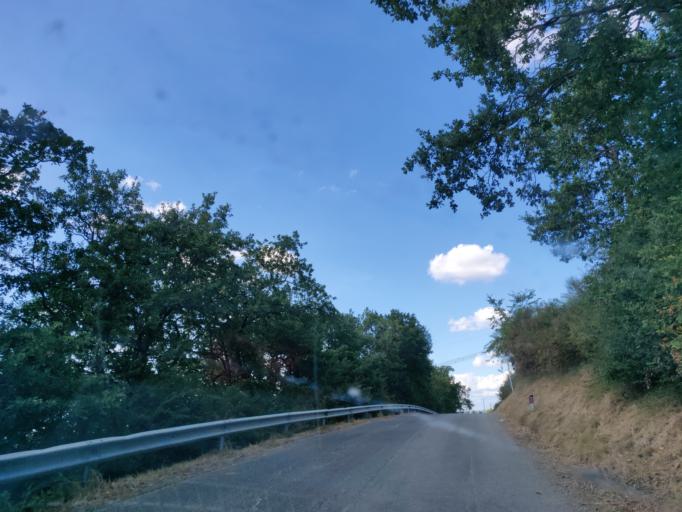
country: IT
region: Tuscany
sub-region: Provincia di Siena
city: Radicofani
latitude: 42.9594
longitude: 11.7267
